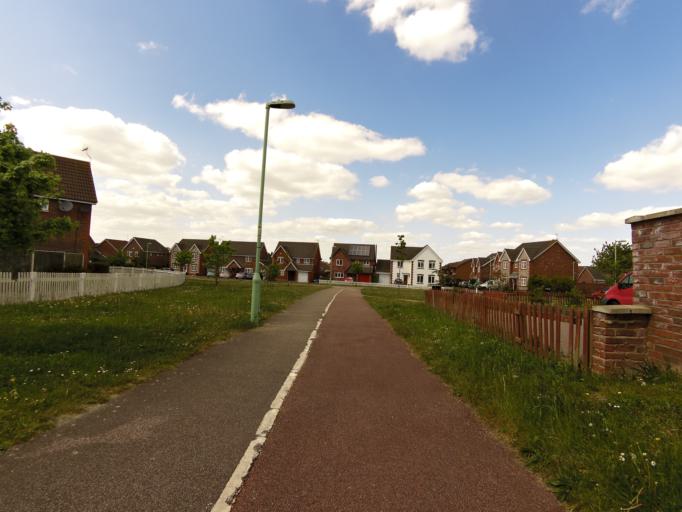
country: GB
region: England
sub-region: Suffolk
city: Kessingland
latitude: 52.4498
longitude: 1.7101
